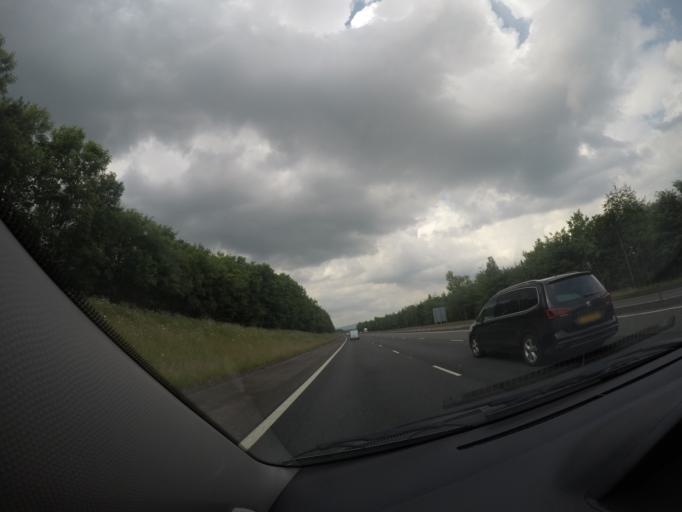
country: GB
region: Scotland
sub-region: Dumfries and Galloway
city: Moffat
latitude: 55.2484
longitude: -3.4098
